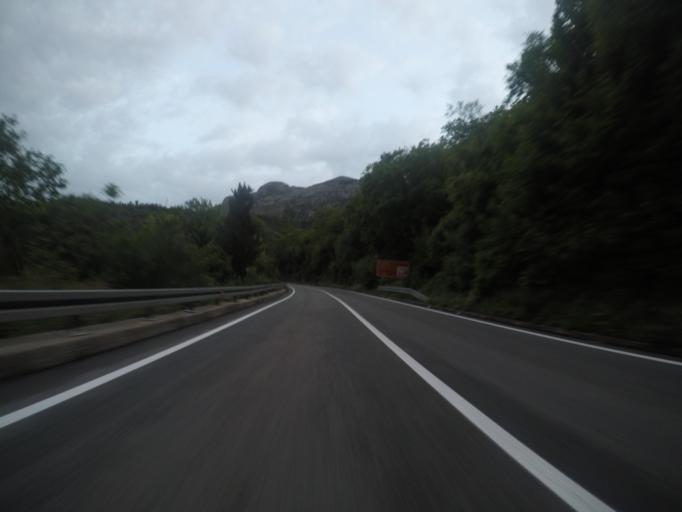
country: ME
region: Bar
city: Sutomore
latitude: 42.1720
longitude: 19.0085
